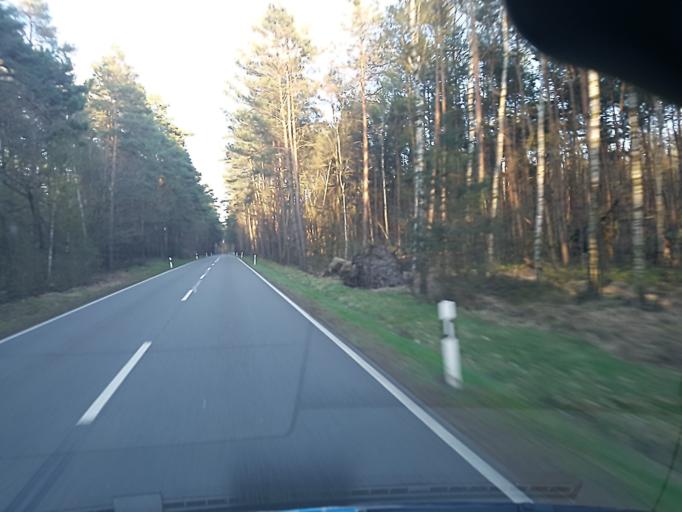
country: DE
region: Saxony
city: Trossin
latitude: 51.5668
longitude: 12.8099
